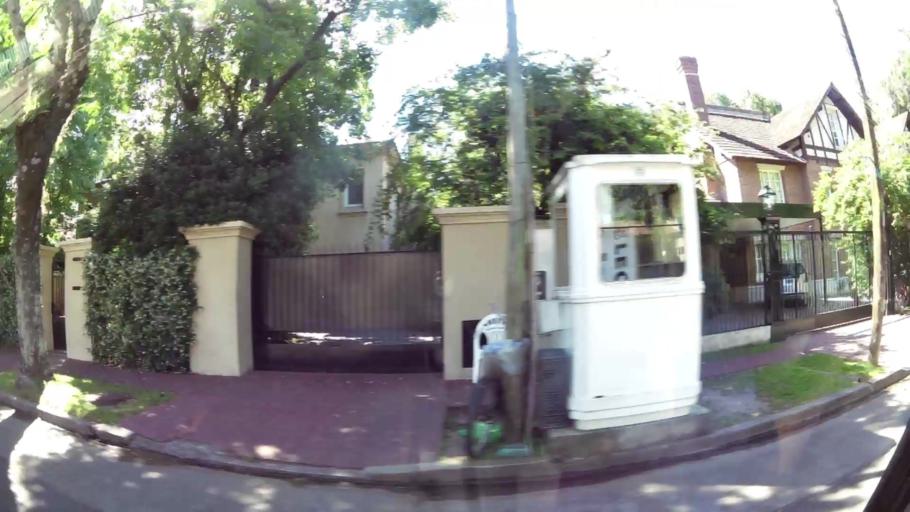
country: AR
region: Buenos Aires
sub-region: Partido de San Isidro
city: San Isidro
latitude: -34.4588
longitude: -58.5272
